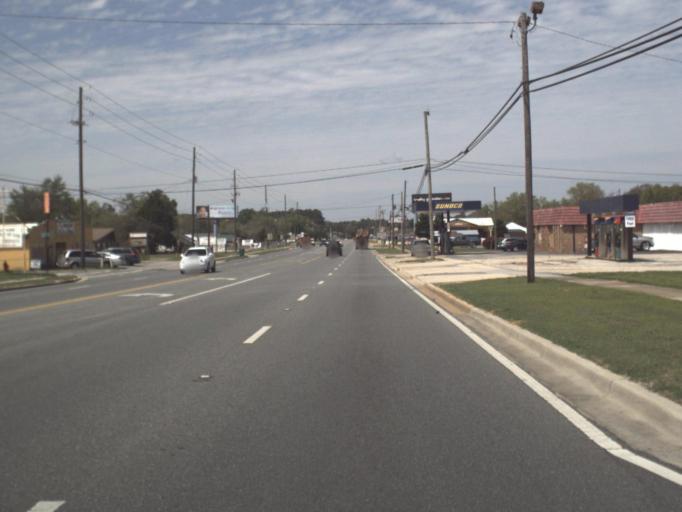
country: US
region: Florida
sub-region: Okaloosa County
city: Crestview
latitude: 30.7652
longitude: -86.5894
